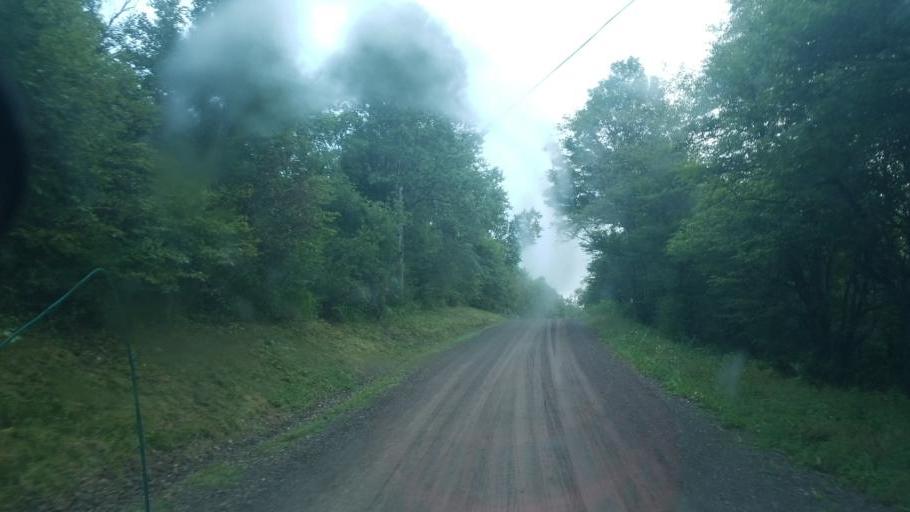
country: US
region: Pennsylvania
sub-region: Potter County
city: Galeton
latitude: 41.8436
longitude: -77.7965
